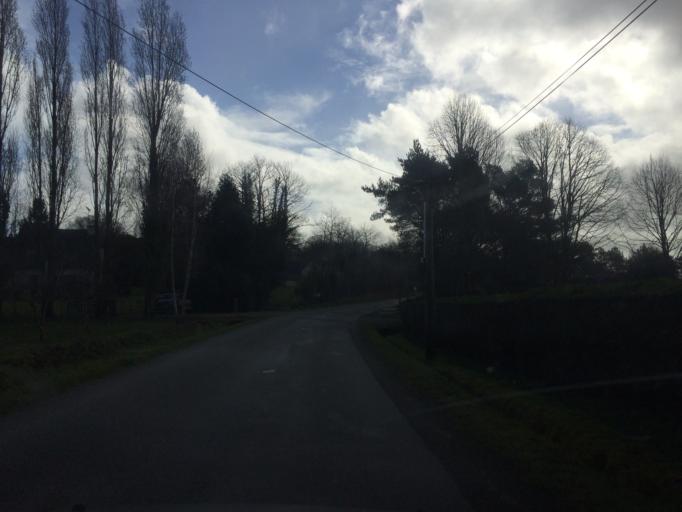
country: FR
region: Brittany
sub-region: Departement du Morbihan
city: Saint-Jean-la-Poterie
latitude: 47.6315
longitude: -2.1198
